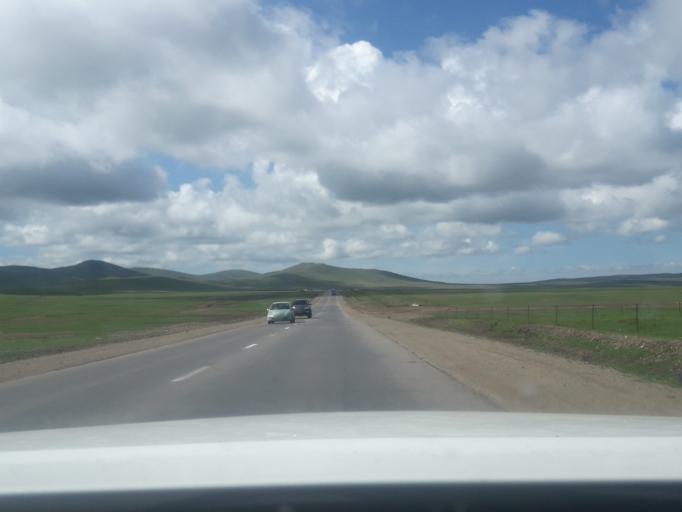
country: MN
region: Central Aimak
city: Altanbulag
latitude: 47.9003
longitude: 106.4596
